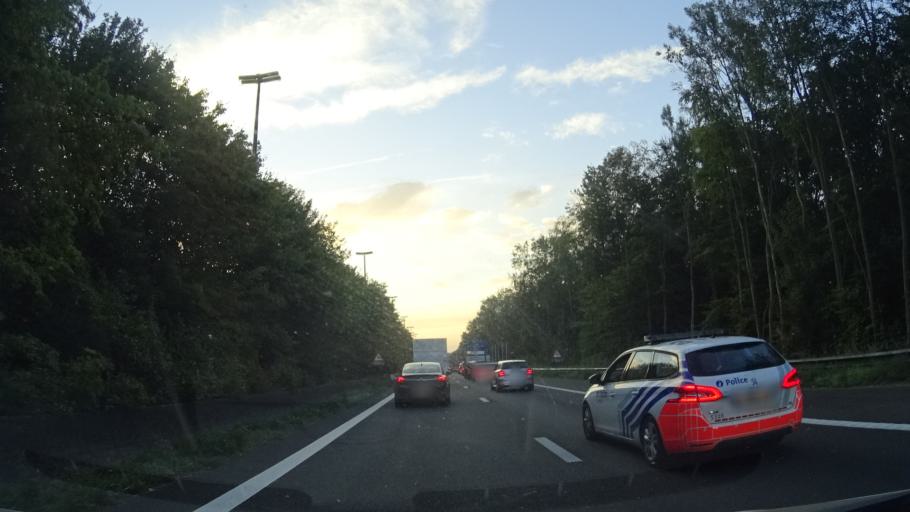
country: BE
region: Wallonia
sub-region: Province du Hainaut
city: Hensies
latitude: 50.4854
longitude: 3.7116
